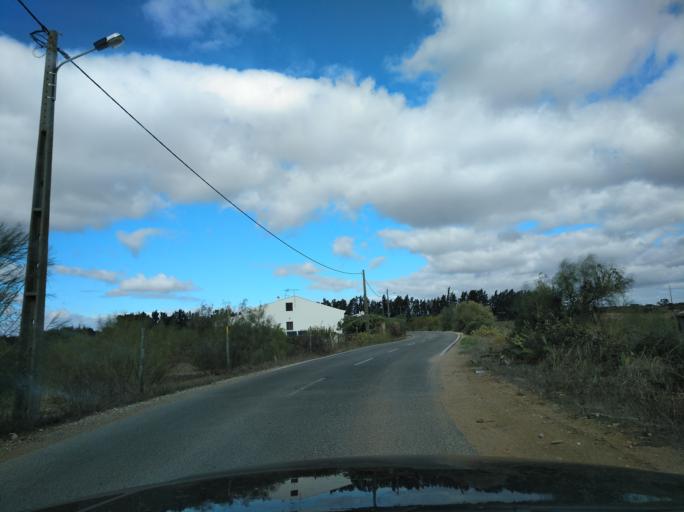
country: PT
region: Faro
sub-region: Vila Real de Santo Antonio
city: Monte Gordo
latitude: 37.1835
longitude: -7.4953
